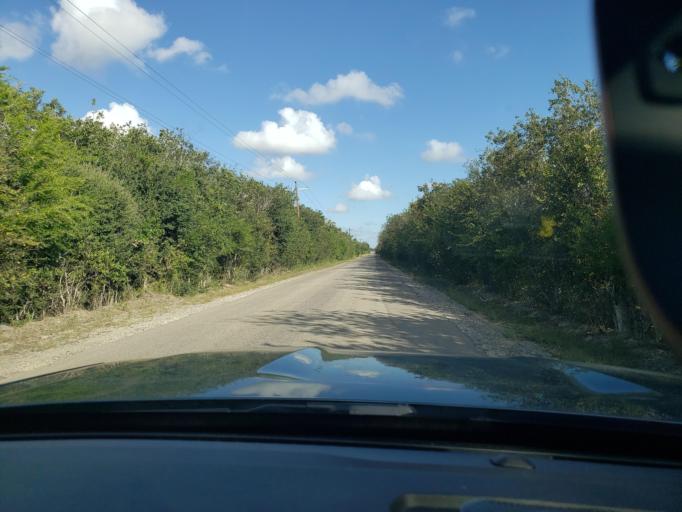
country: US
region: Texas
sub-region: Bee County
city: Beeville
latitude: 28.4492
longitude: -97.7170
